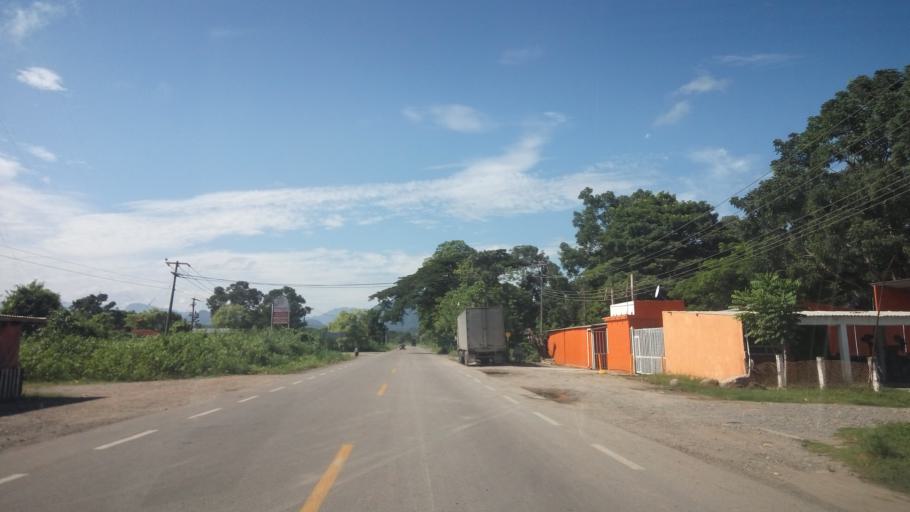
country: MX
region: Tabasco
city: Teapa
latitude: 17.5906
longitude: -92.9659
